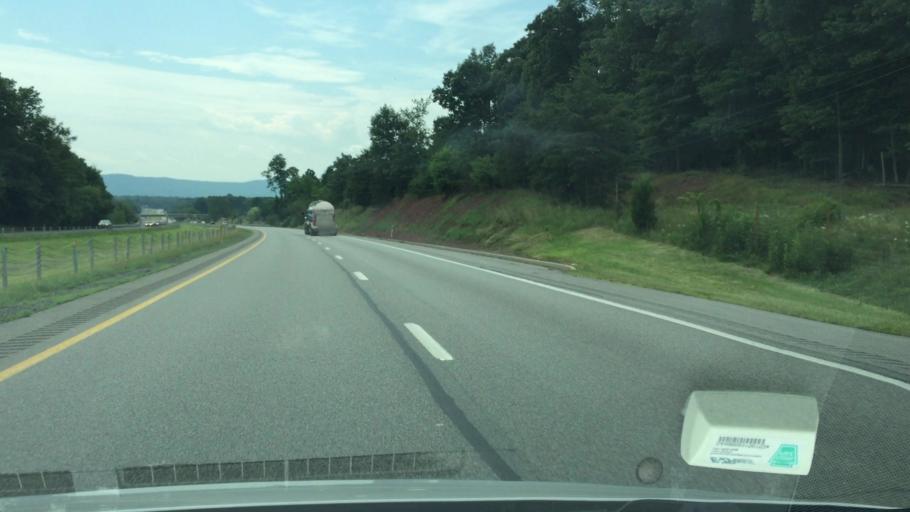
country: US
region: Maryland
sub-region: Washington County
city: Hancock
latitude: 39.8375
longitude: -78.2763
